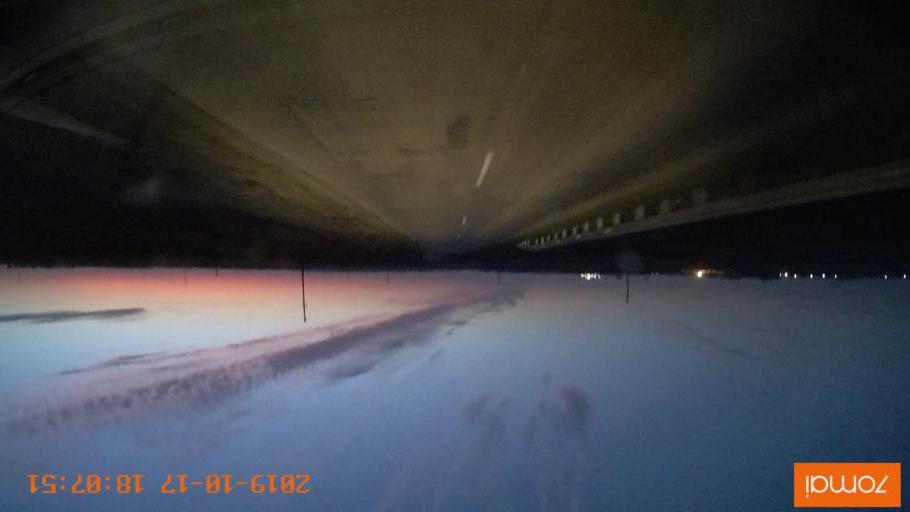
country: RU
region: Tula
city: Kurkino
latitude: 53.4401
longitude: 38.6484
